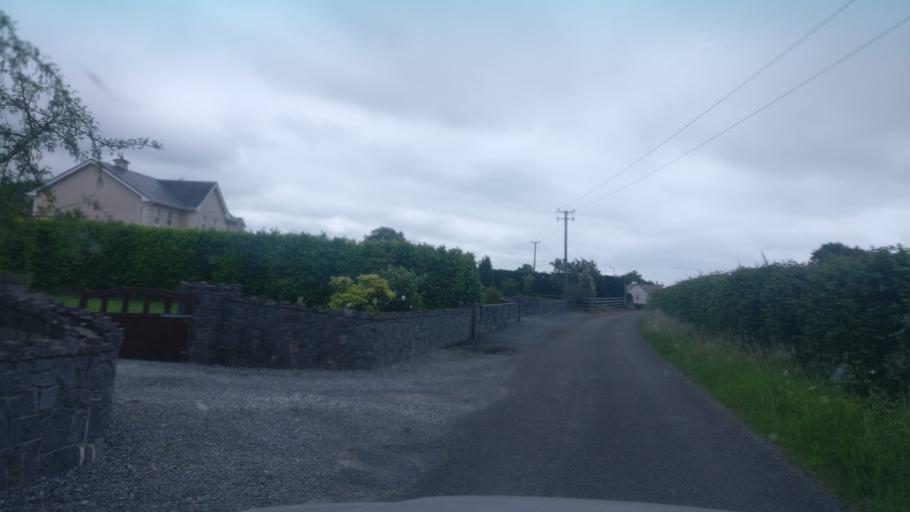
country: IE
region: Connaught
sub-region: County Galway
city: Ballinasloe
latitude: 53.2925
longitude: -8.3397
